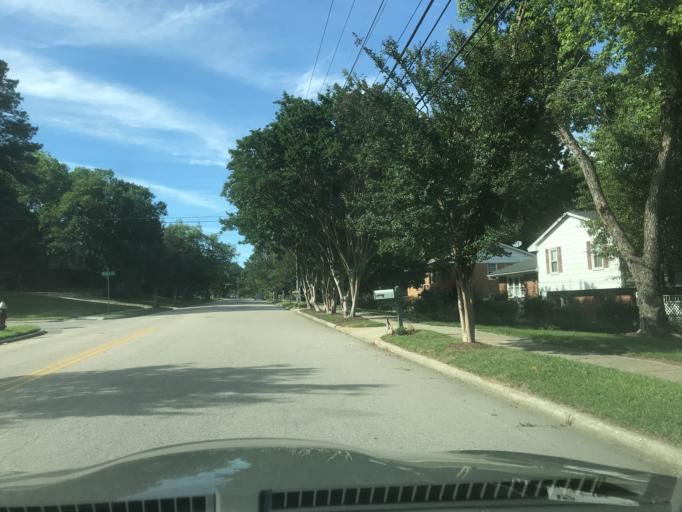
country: US
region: North Carolina
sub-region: Wake County
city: Raleigh
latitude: 35.8329
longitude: -78.5993
